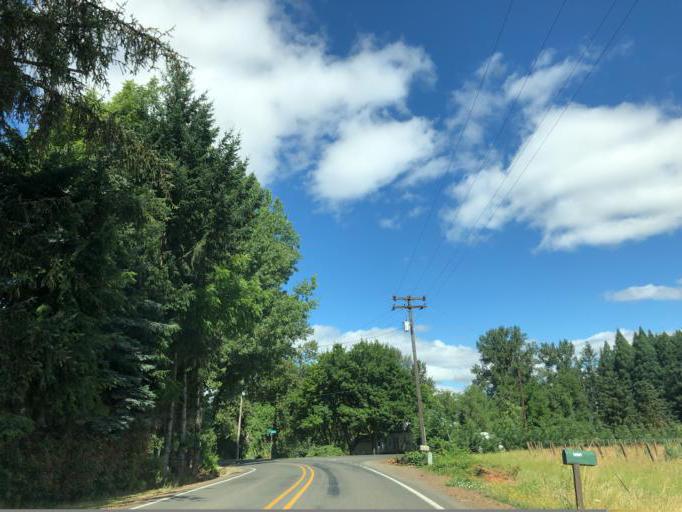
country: US
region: Oregon
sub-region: Marion County
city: Mount Angel
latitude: 45.1012
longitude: -122.7446
